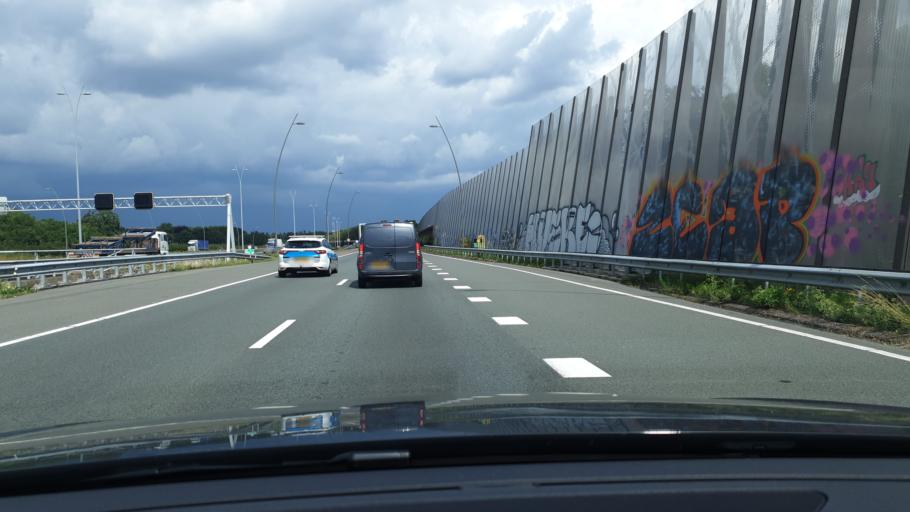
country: NL
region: North Brabant
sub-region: Gemeente Eindhoven
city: Meerhoven
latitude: 51.4414
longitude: 5.4276
